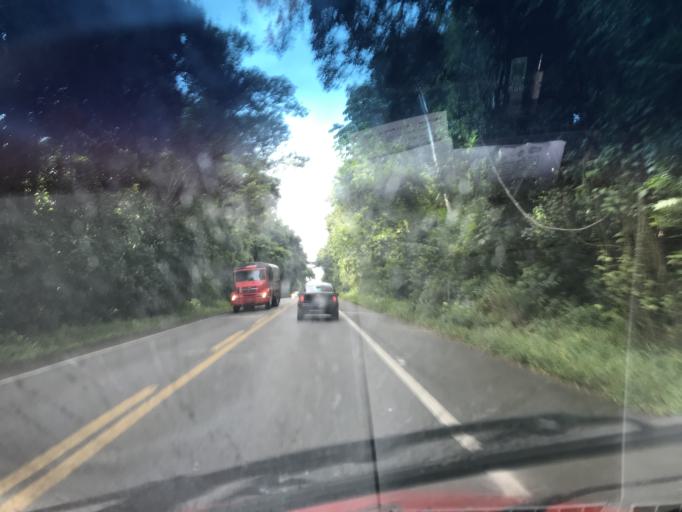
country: BR
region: Bahia
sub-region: Itajuipe
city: Itajuipe
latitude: -14.6313
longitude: -39.3341
